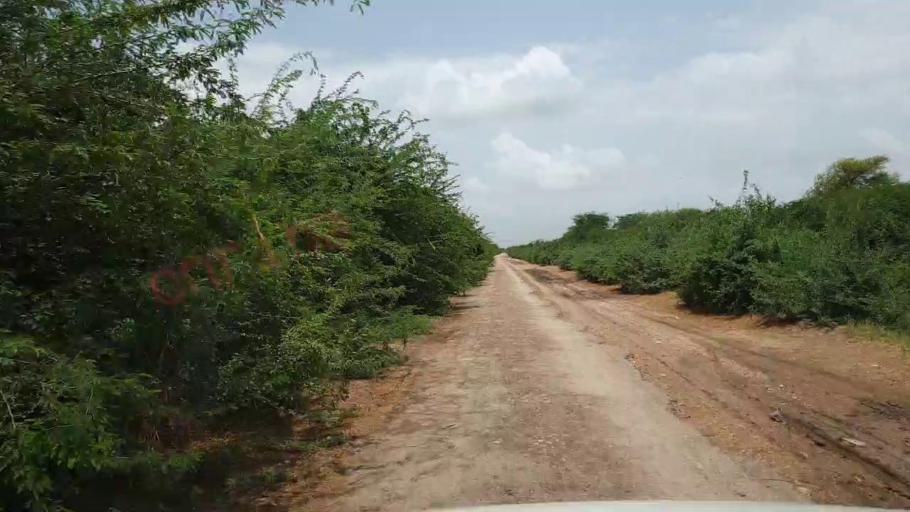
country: PK
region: Sindh
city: Kario
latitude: 24.7168
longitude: 68.5819
